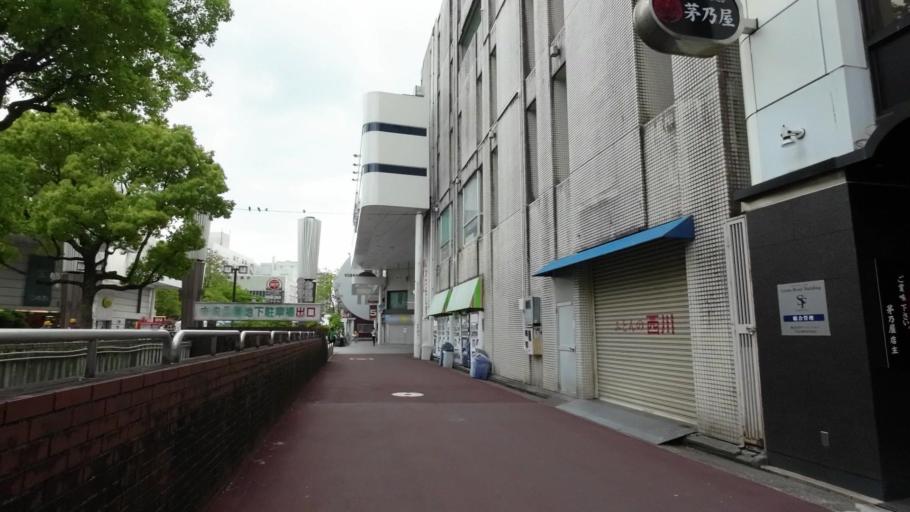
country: JP
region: Kochi
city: Kochi-shi
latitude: 33.5611
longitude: 133.5403
